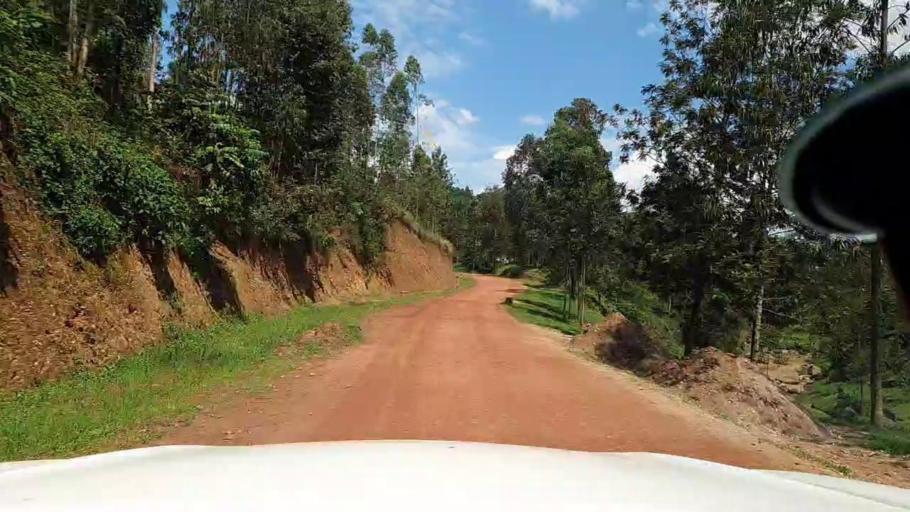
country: RW
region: Kigali
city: Kigali
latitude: -1.7720
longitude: 29.8741
